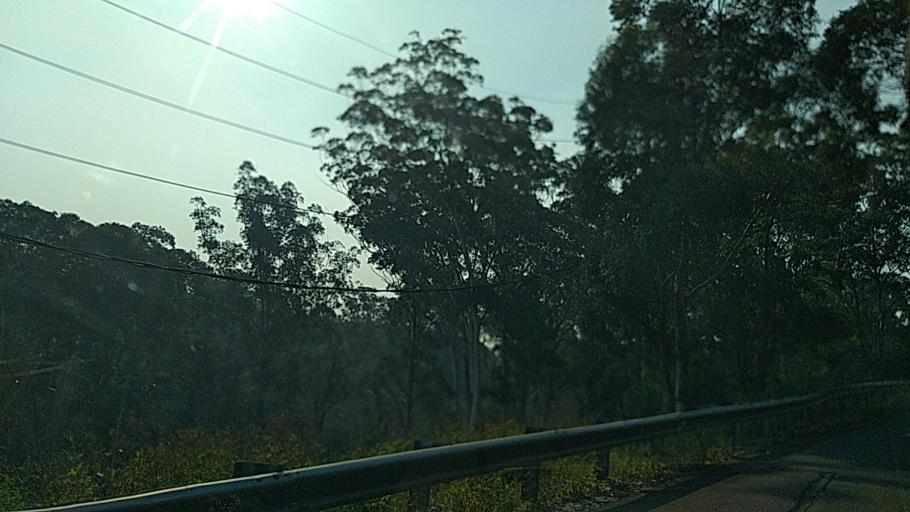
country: AU
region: New South Wales
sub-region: Wollondilly
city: Douglas Park
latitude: -34.2271
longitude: 150.7445
